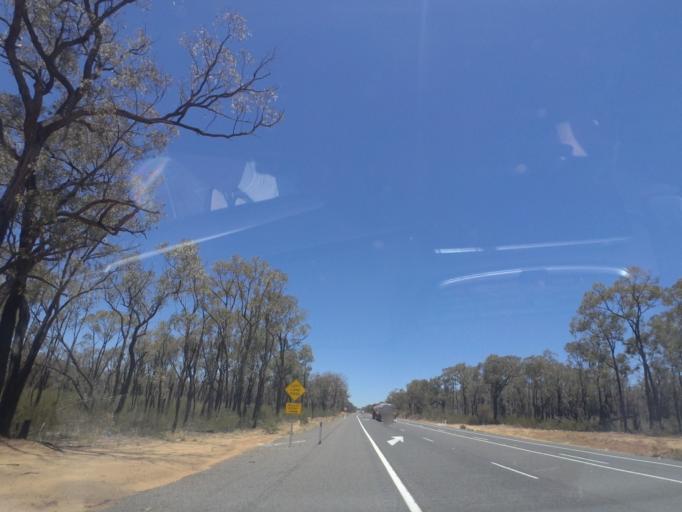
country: AU
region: New South Wales
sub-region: Warrumbungle Shire
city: Coonabarabran
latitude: -30.9037
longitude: 149.4383
